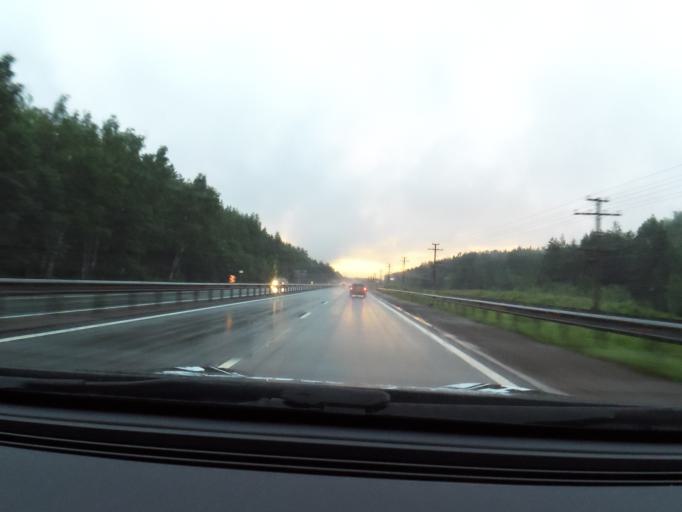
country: RU
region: Tatarstan
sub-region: Tukayevskiy Rayon
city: Naberezhnyye Chelny
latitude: 55.7390
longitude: 52.2498
